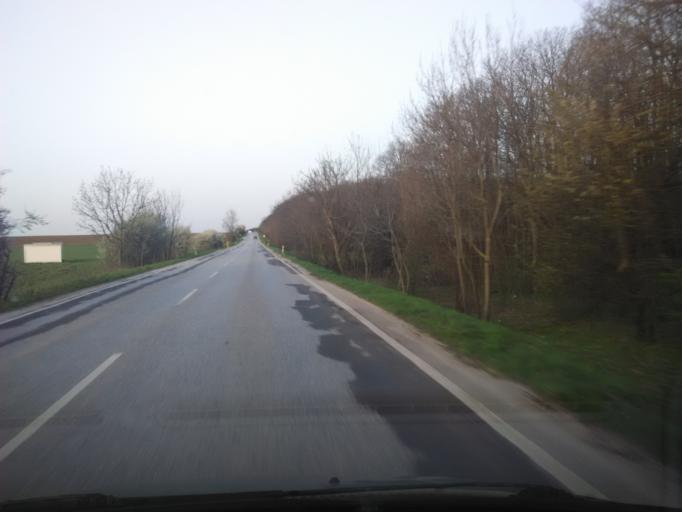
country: SK
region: Nitriansky
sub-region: Okres Nitra
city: Nitra
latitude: 48.2722
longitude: 18.0484
